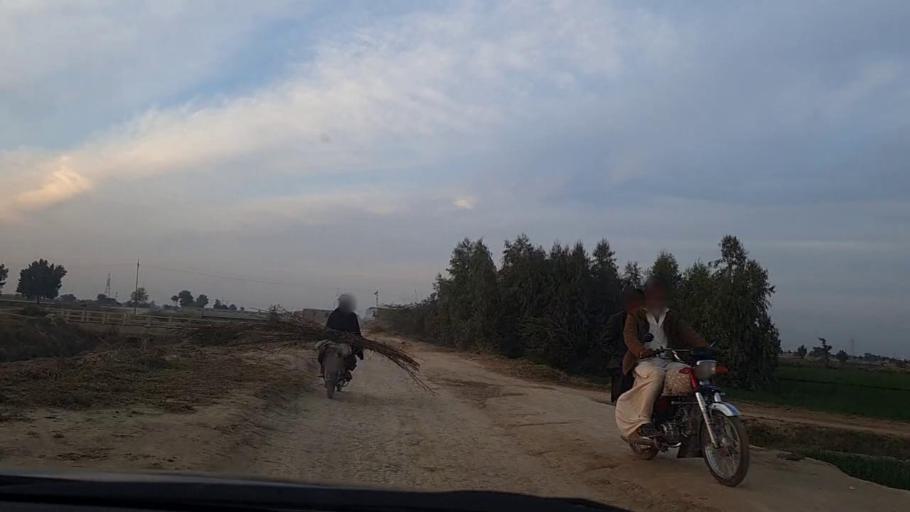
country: PK
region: Sindh
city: Sakrand
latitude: 26.2089
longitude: 68.3257
